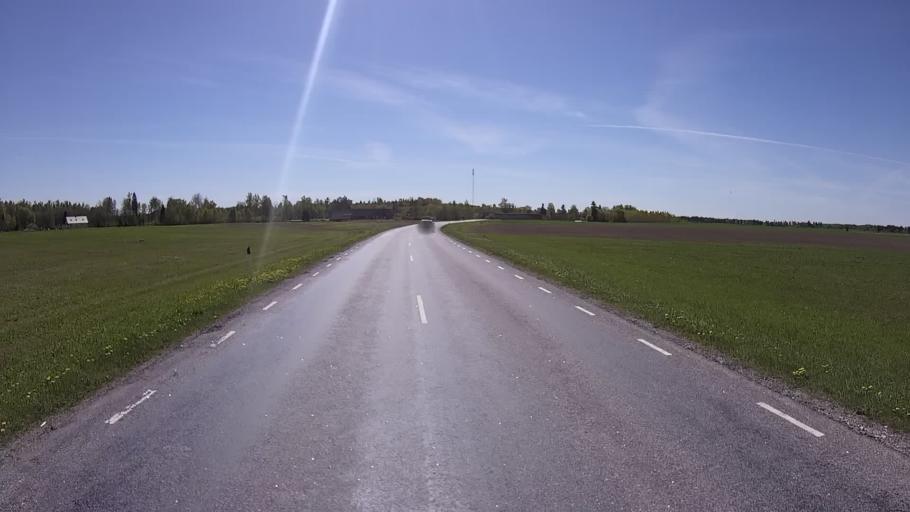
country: EE
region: Harju
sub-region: Raasiku vald
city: Raasiku
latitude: 59.0754
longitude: 25.1640
